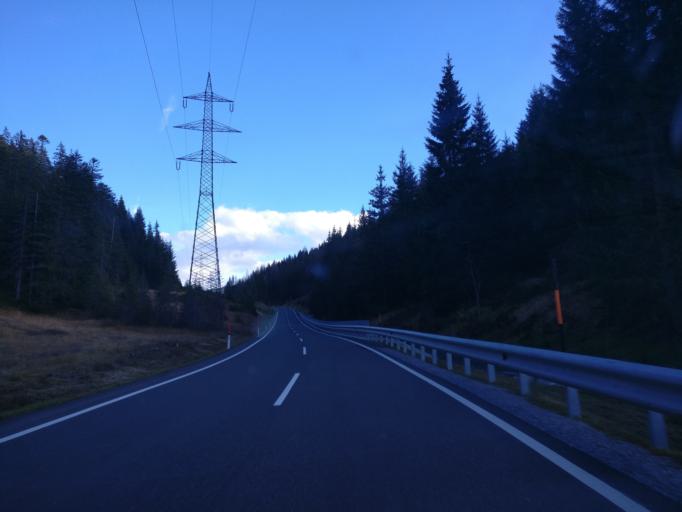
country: AT
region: Salzburg
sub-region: Politischer Bezirk Zell am See
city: Dienten am Hochkonig
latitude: 47.3992
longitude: 12.9963
